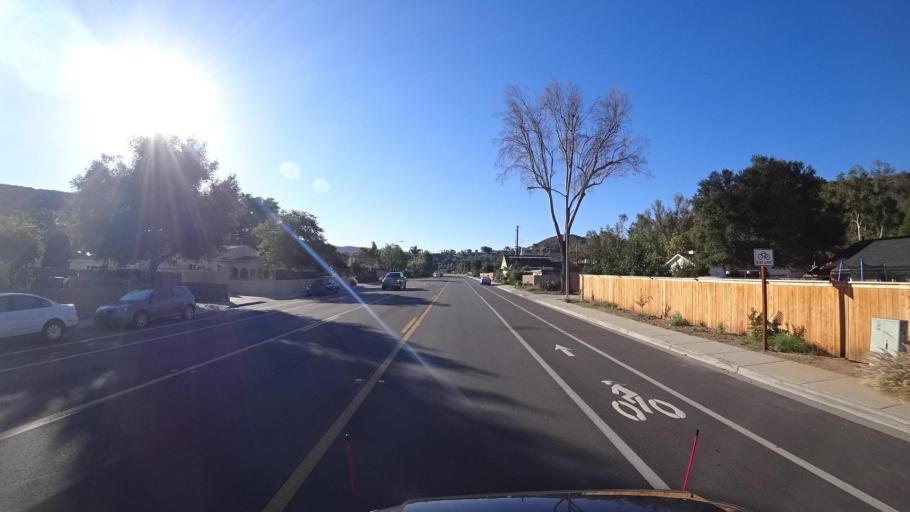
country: US
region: California
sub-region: San Diego County
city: Lakeside
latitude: 32.8445
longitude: -116.9162
